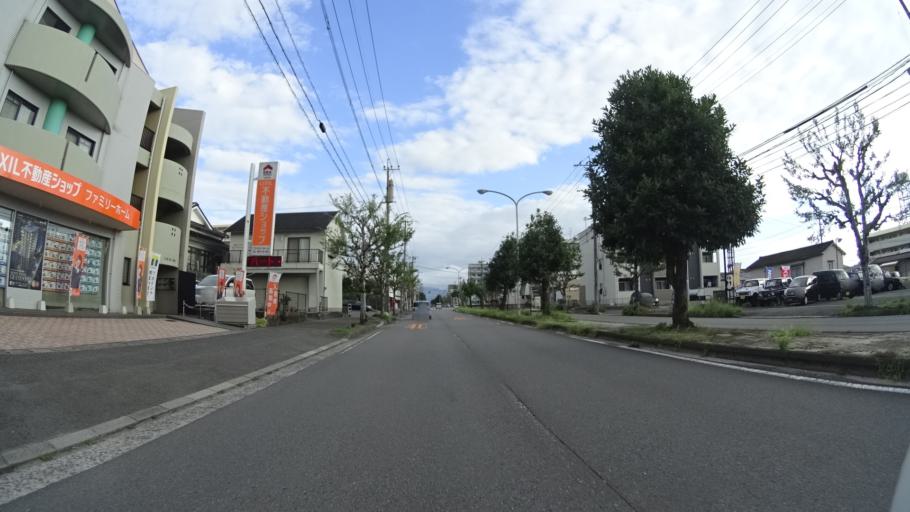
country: JP
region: Oita
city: Beppu
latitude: 33.2908
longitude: 131.4960
